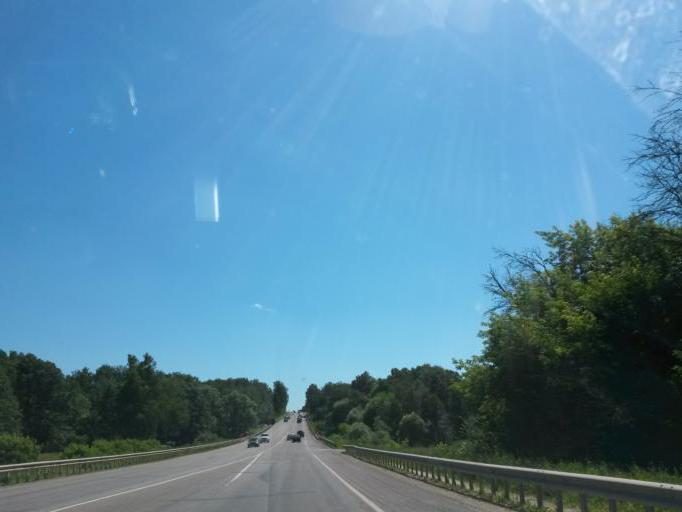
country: RU
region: Moskovskaya
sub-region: Chekhovskiy Rayon
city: Chekhov
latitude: 55.1110
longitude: 37.4471
